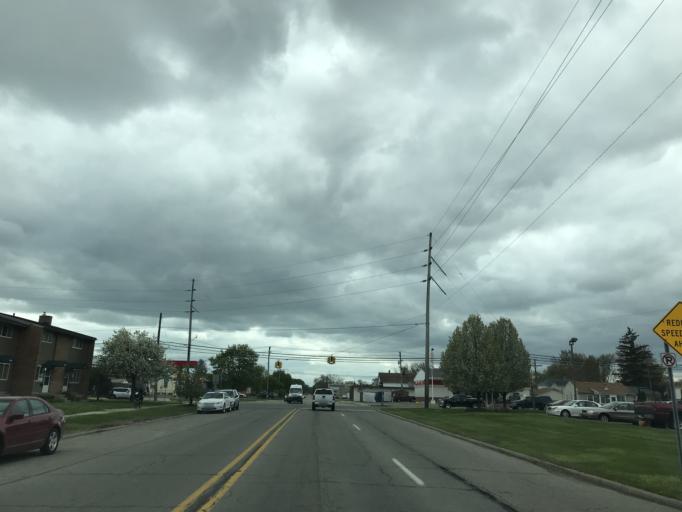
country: US
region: Michigan
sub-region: Wayne County
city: Riverview
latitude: 42.1858
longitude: -83.1796
